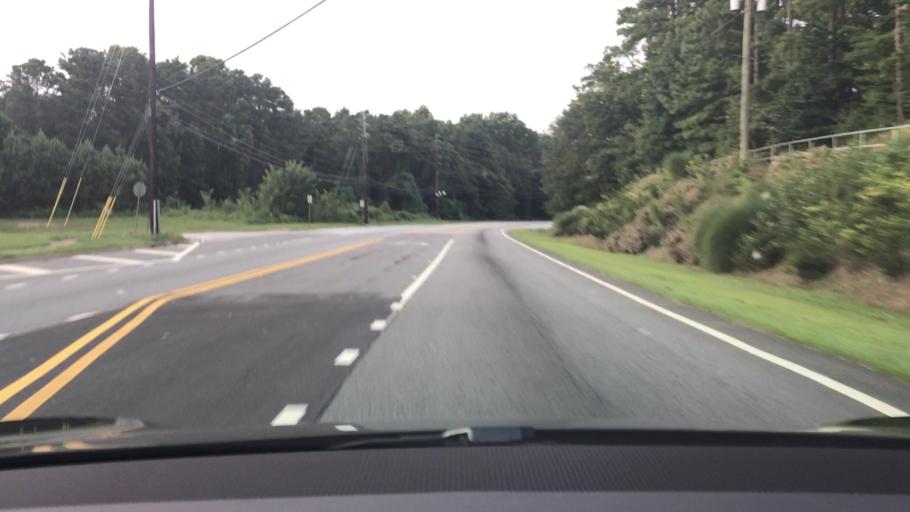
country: US
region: Georgia
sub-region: Gwinnett County
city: Duluth
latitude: 34.0102
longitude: -84.1303
